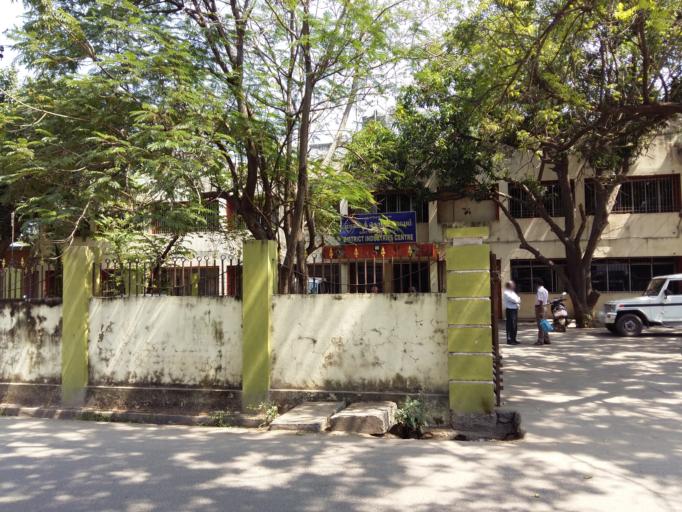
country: IN
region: Pondicherry
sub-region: Puducherry
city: Puducherry
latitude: 11.9437
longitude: 79.8044
